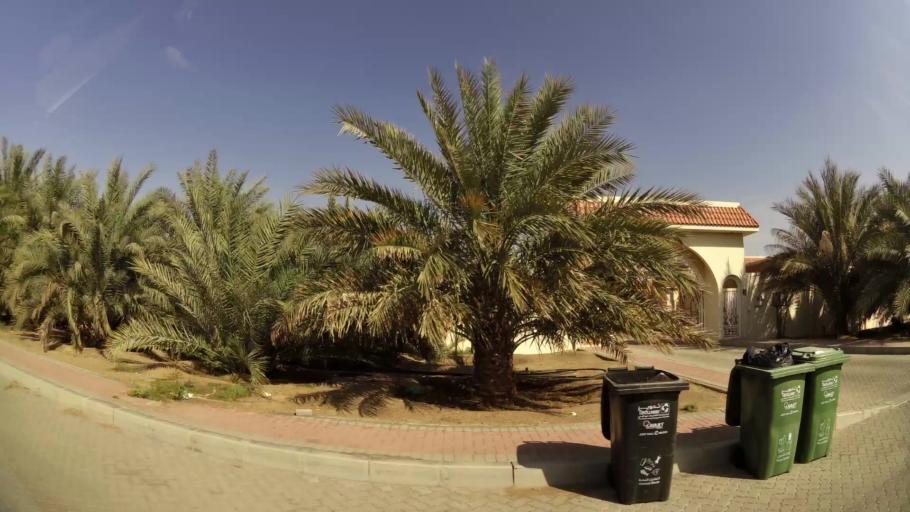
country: AE
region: Abu Dhabi
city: Al Ain
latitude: 24.0891
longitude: 55.9274
